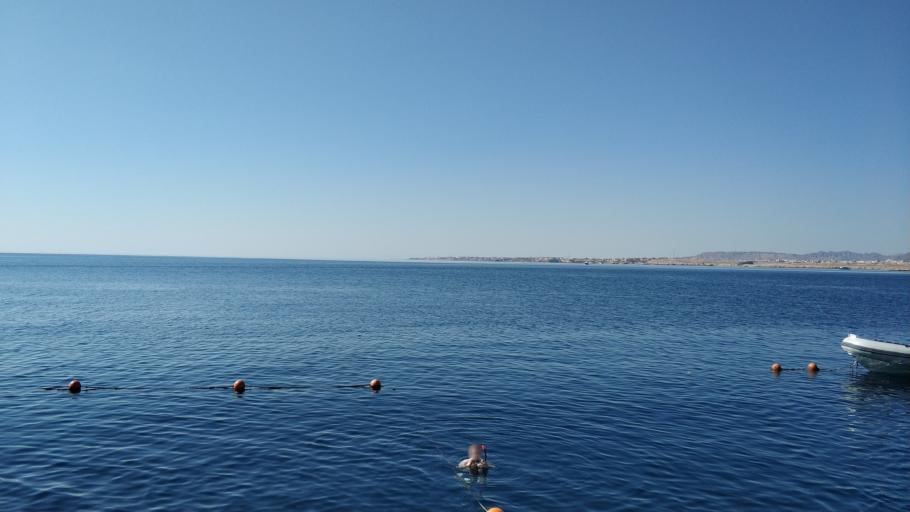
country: EG
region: South Sinai
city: Sharm el-Sheikh
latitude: 27.9148
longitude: 34.3610
